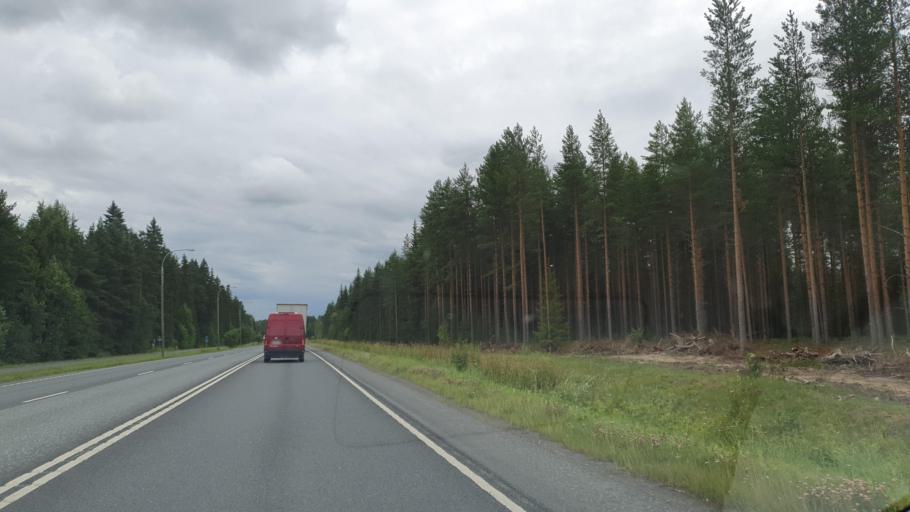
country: FI
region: Northern Savo
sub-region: Ylae-Savo
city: Iisalmi
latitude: 63.4756
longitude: 27.2989
